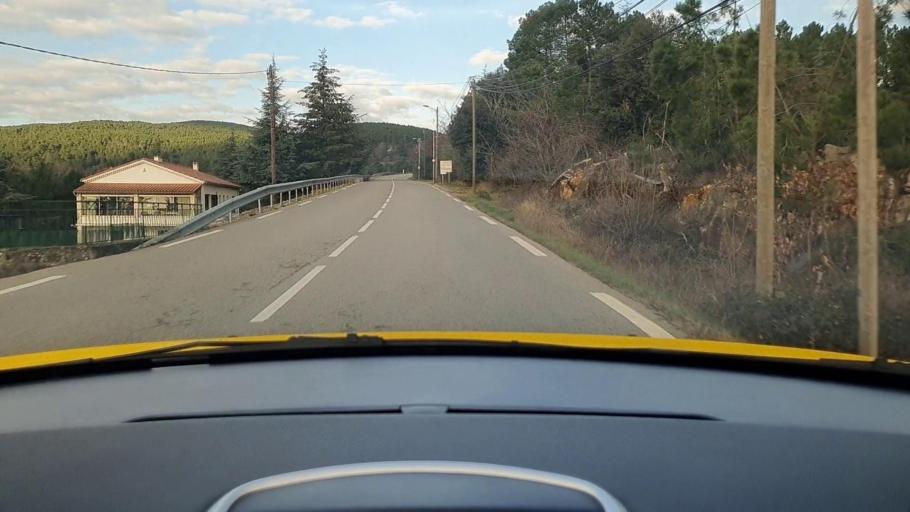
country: FR
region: Languedoc-Roussillon
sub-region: Departement du Gard
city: Les Salles-du-Gardon
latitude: 44.2634
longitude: 4.0332
